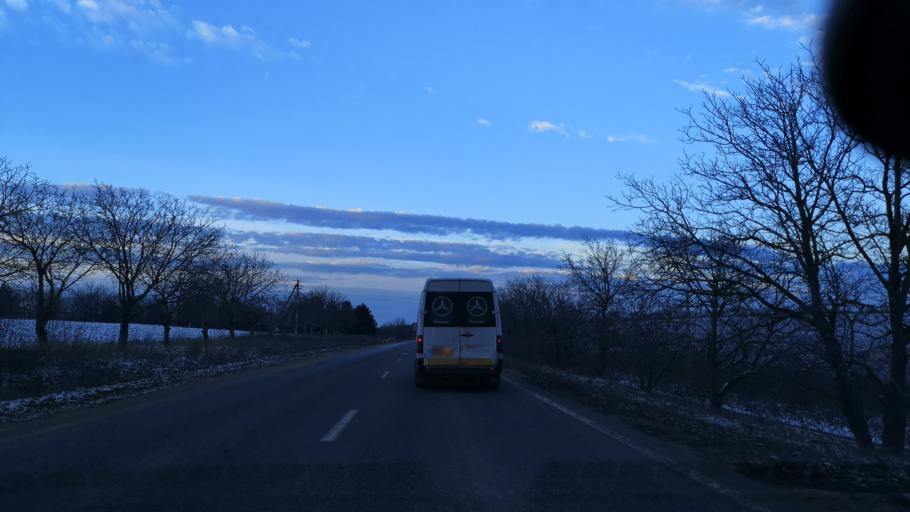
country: MD
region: Orhei
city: Orhei
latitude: 47.5457
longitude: 28.7927
